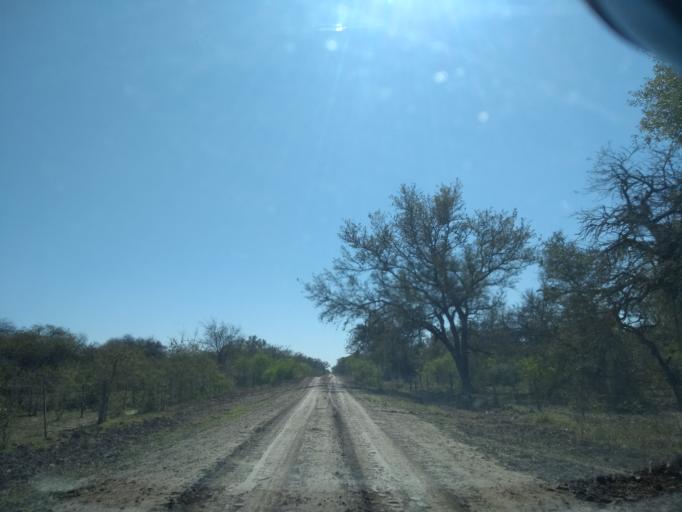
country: AR
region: Chaco
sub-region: Departamento de Quitilipi
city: Quitilipi
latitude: -26.7296
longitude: -60.2312
